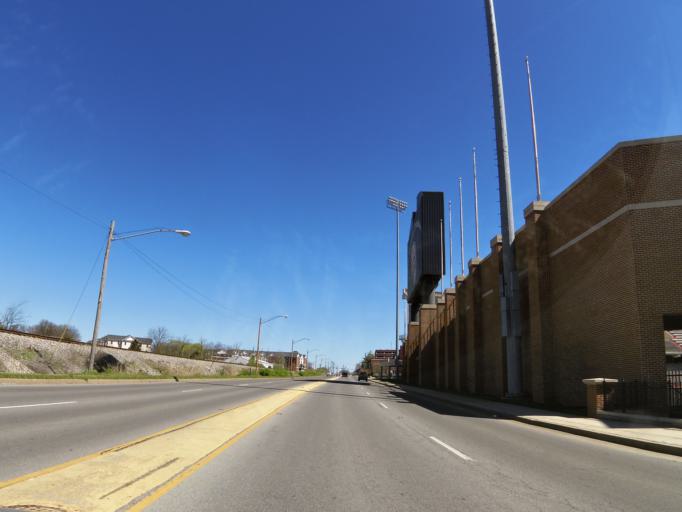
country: US
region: Kentucky
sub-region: Warren County
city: Bowling Green
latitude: 36.9848
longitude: -86.4608
